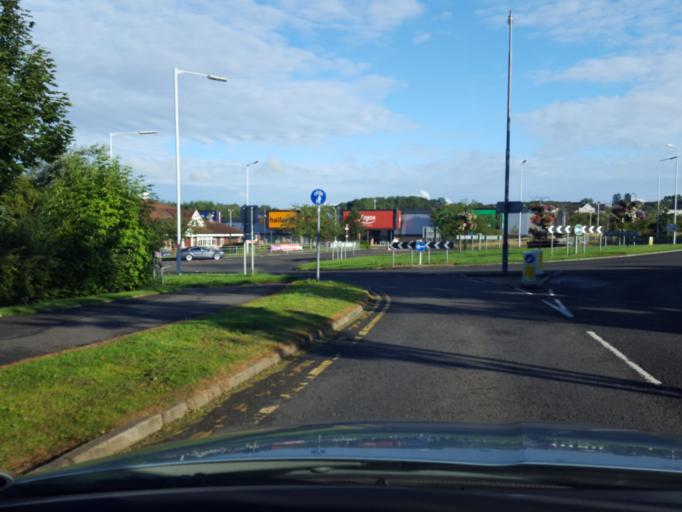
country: GB
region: Scotland
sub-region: Fife
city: Crossgates
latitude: 56.0801
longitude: -3.4062
